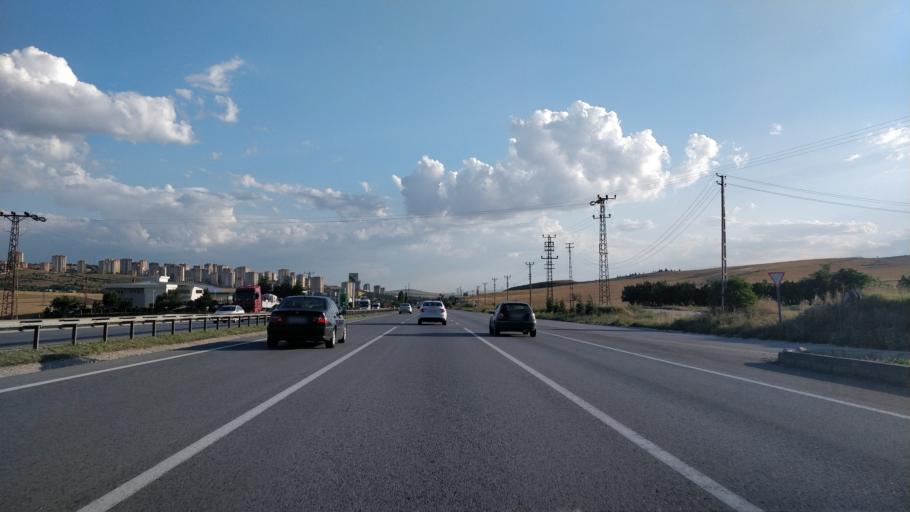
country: TR
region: Ankara
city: Etimesgut
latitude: 39.8358
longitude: 32.5851
